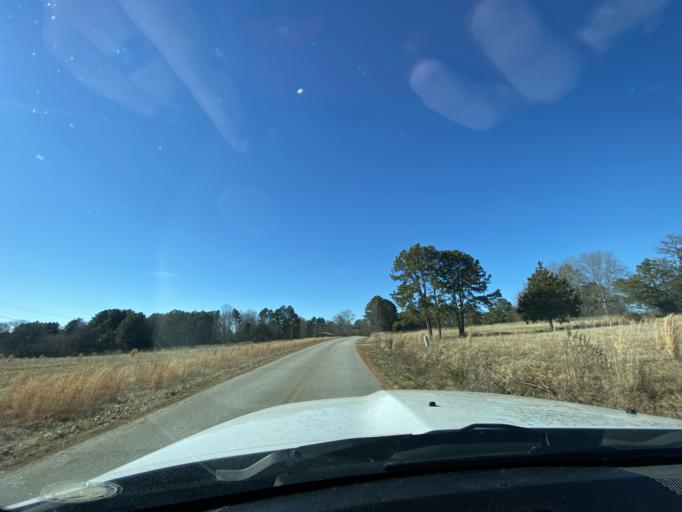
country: US
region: South Carolina
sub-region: Pickens County
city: Liberty
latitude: 34.8312
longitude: -82.7074
